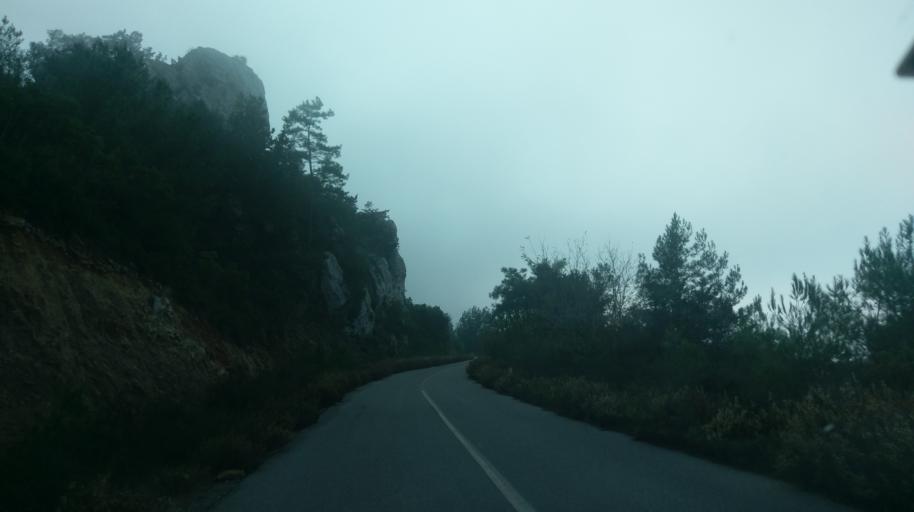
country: CY
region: Ammochostos
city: Trikomo
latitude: 35.3846
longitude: 33.8783
